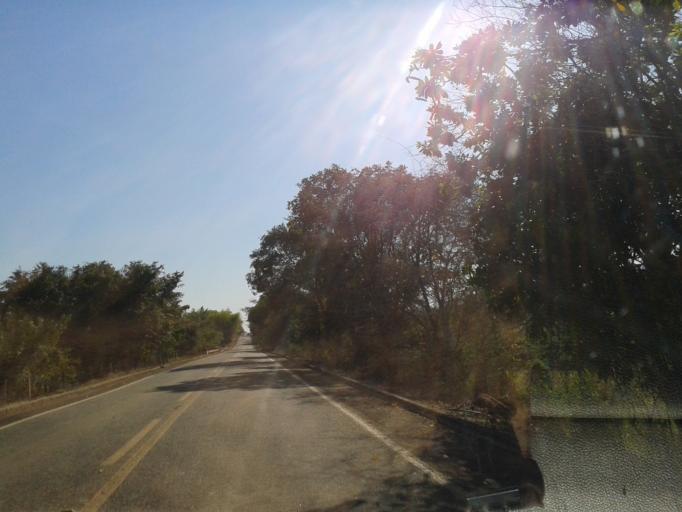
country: BR
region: Goias
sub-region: Mozarlandia
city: Mozarlandia
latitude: -14.5734
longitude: -50.5017
